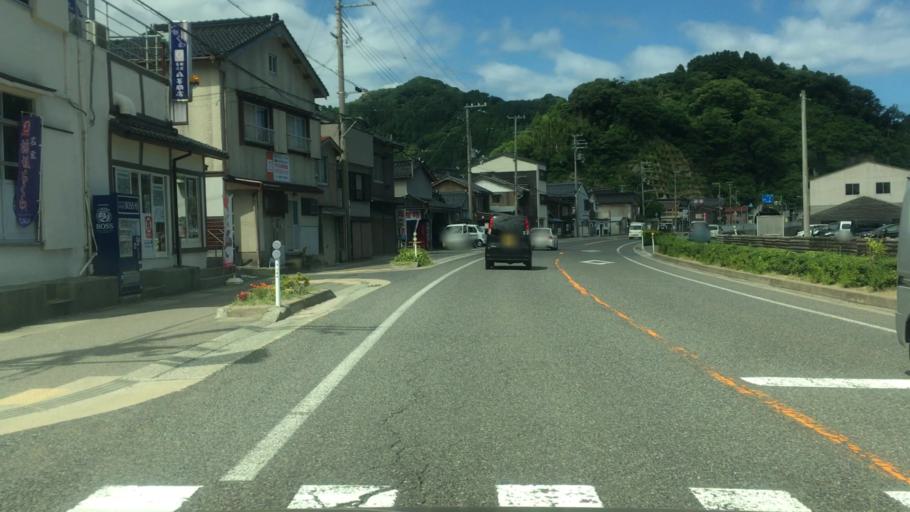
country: JP
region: Tottori
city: Tottori
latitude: 35.6201
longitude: 134.4326
